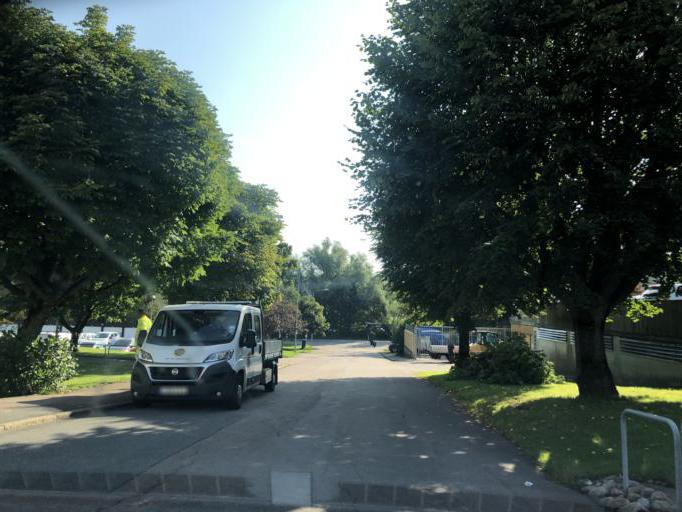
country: SE
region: Vaestra Goetaland
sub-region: Goteborg
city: Goeteborg
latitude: 57.7527
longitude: 11.9888
